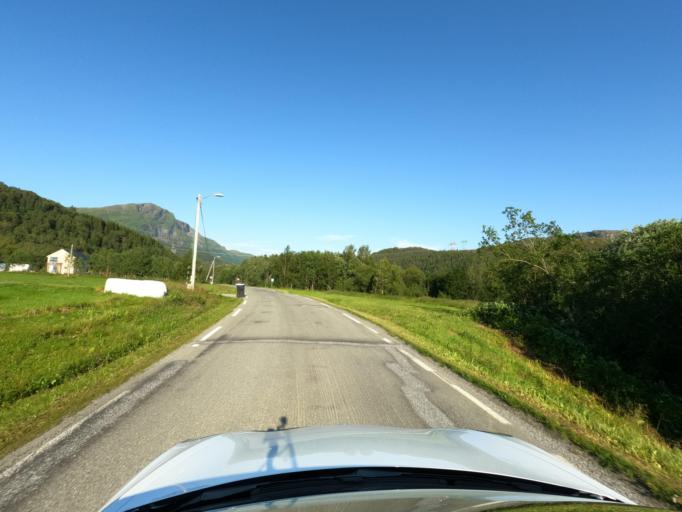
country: NO
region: Nordland
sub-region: Narvik
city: Bjerkvik
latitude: 68.5564
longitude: 17.6143
